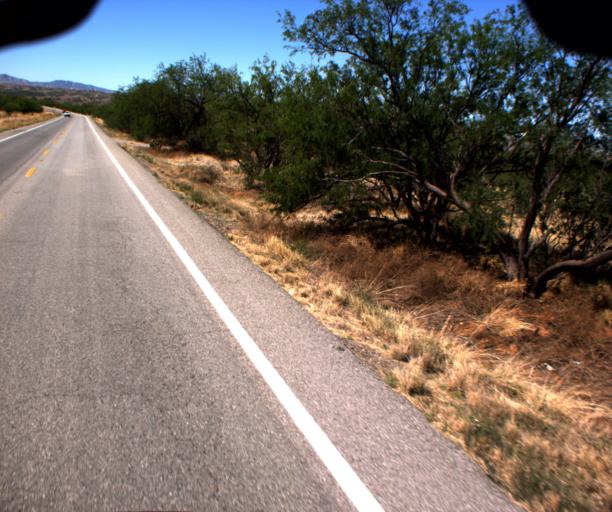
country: US
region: Arizona
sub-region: Santa Cruz County
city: Nogales
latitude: 31.4097
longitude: -110.8616
